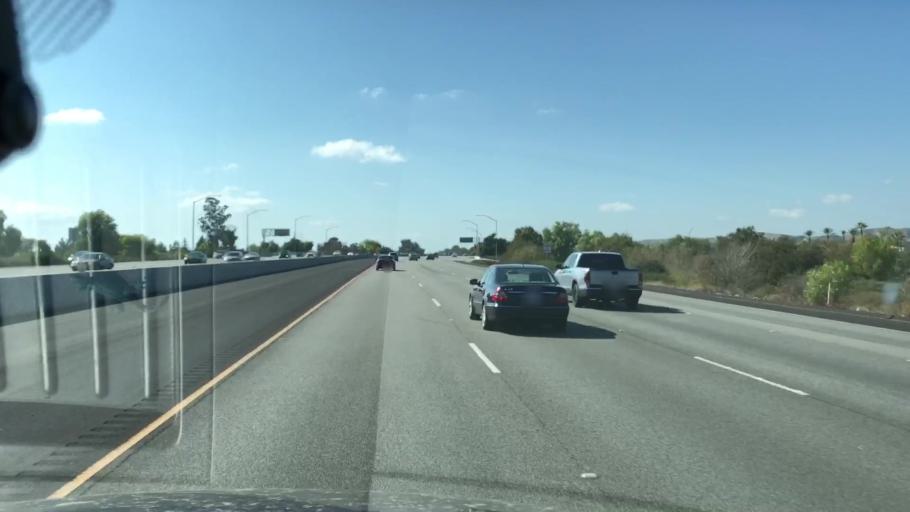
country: US
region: California
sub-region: Ventura County
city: Santa Susana
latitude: 34.2819
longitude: -118.7149
